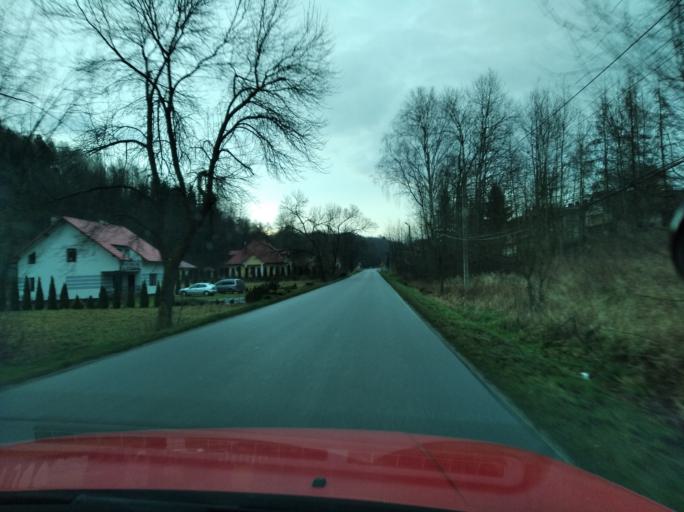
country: PL
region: Subcarpathian Voivodeship
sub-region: Powiat strzyzowski
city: Gwoznica Gorna
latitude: 49.8385
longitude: 21.9858
